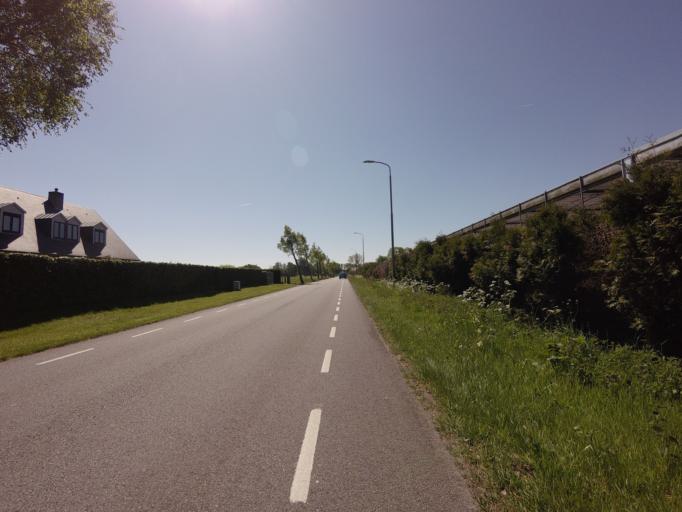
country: BE
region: Flanders
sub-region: Provincie Antwerpen
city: Essen
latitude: 51.4755
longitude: 4.4603
